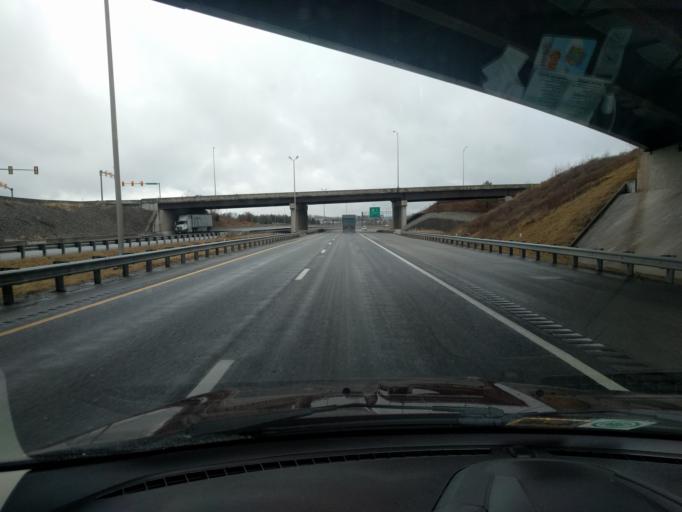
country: US
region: Virginia
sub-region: Montgomery County
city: Merrimac
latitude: 37.1942
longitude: -80.4042
